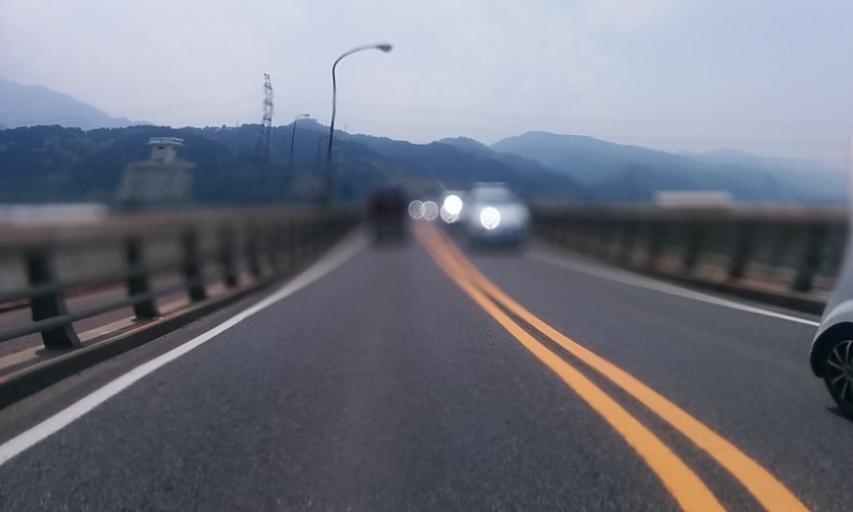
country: JP
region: Ehime
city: Saijo
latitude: 33.9039
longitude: 133.1844
